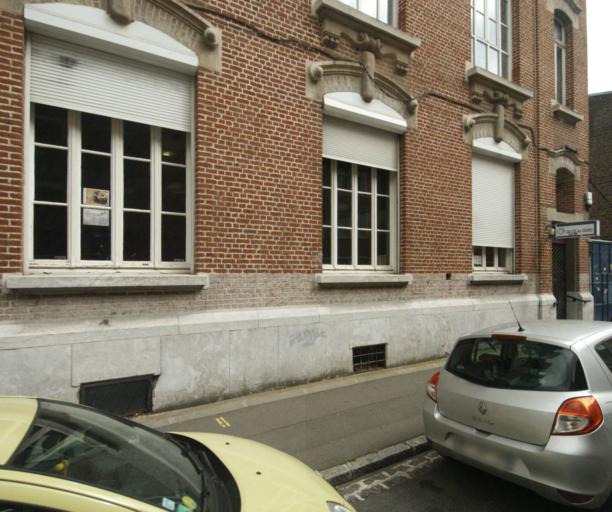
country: FR
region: Nord-Pas-de-Calais
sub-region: Departement du Nord
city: Lille
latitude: 50.6327
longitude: 3.0480
